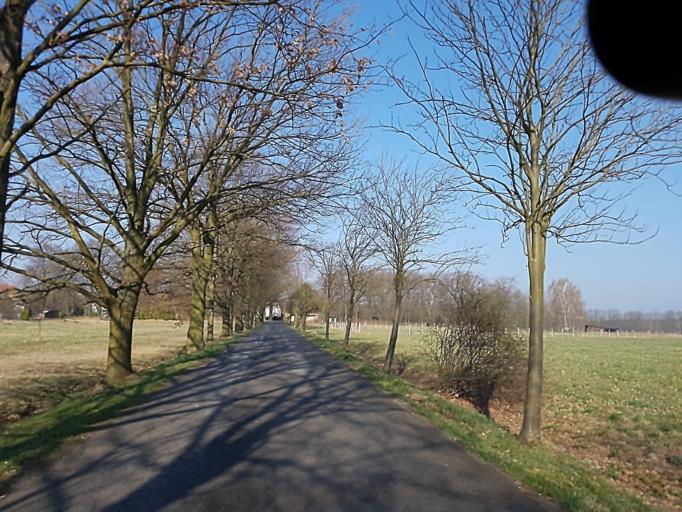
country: DE
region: Brandenburg
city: Tschernitz
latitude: 51.6539
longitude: 14.5862
